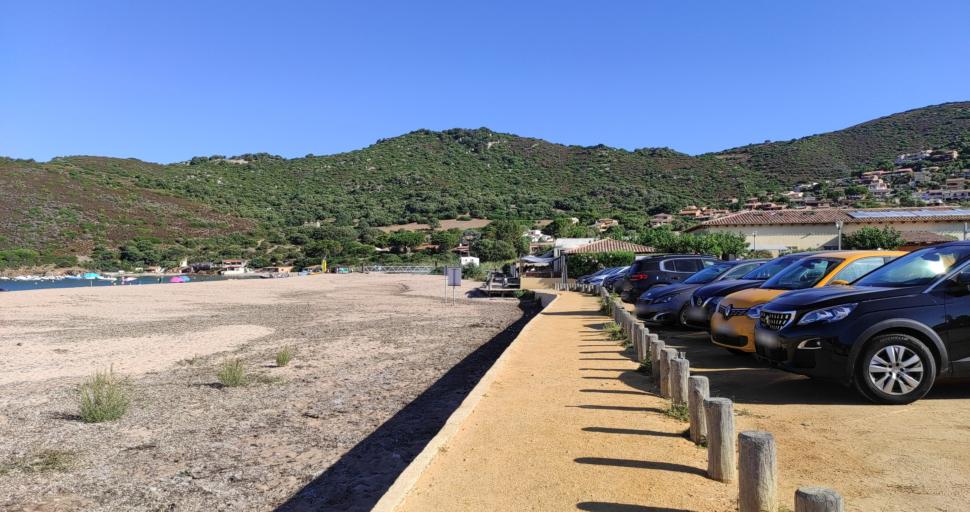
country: FR
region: Corsica
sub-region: Departement de la Corse-du-Sud
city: Alata
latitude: 41.9913
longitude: 8.6696
